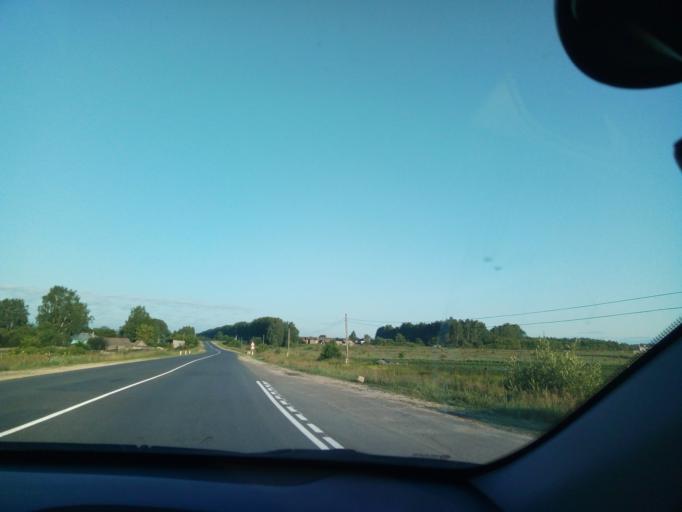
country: RU
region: Nizjnij Novgorod
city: Satis
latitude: 54.9016
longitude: 43.1439
